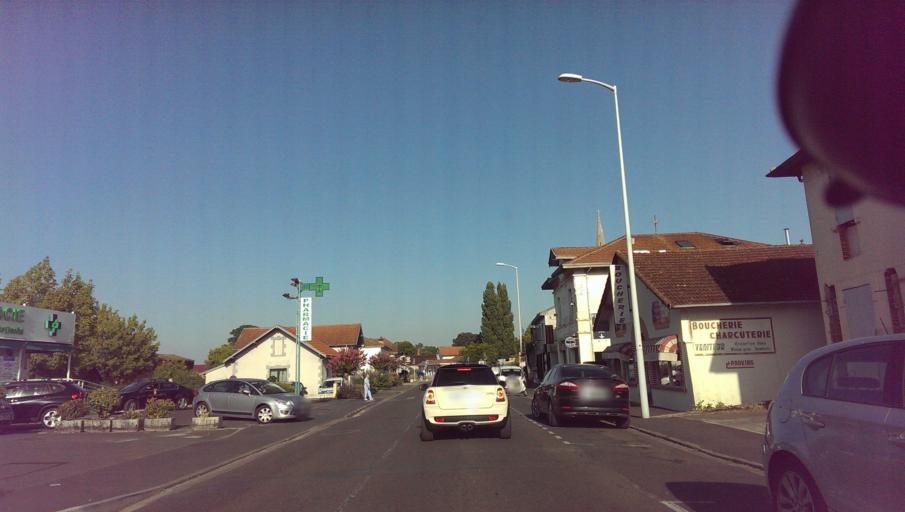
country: FR
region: Aquitaine
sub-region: Departement des Landes
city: Mimizan
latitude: 44.2028
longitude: -1.2312
